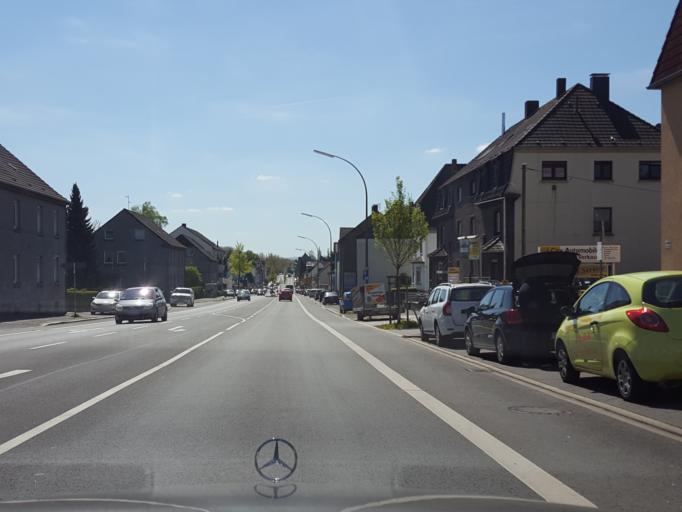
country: DE
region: North Rhine-Westphalia
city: Castrop-Rauxel
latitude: 51.5065
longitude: 7.3243
